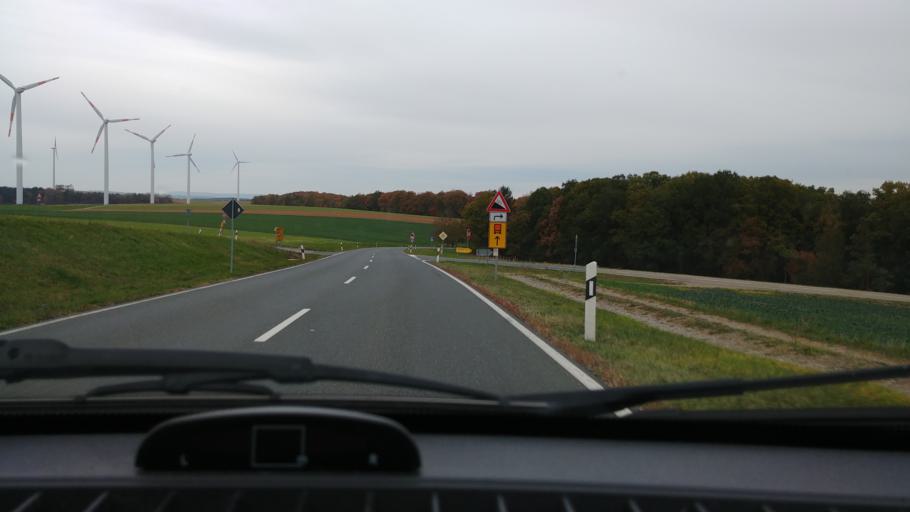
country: DE
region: Bavaria
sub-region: Regierungsbezirk Unterfranken
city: Neubrunn
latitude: 49.7326
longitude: 9.6214
